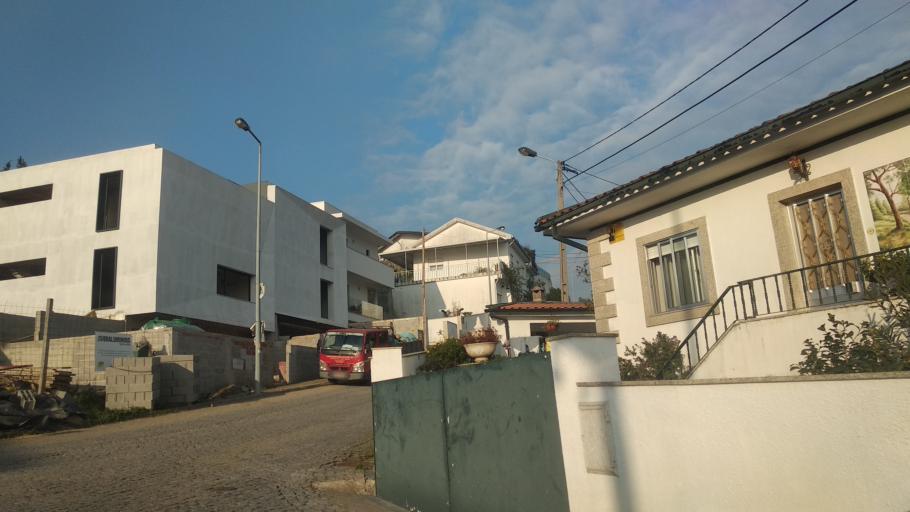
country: PT
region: Braga
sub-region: Braga
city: Adaufe
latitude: 41.5706
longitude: -8.3793
